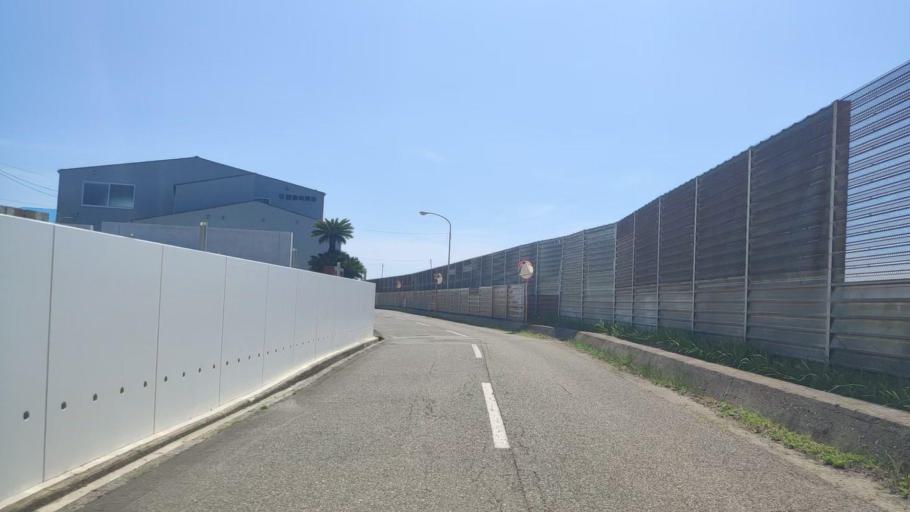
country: JP
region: Ishikawa
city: Kanazawa-shi
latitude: 36.6031
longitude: 136.5891
